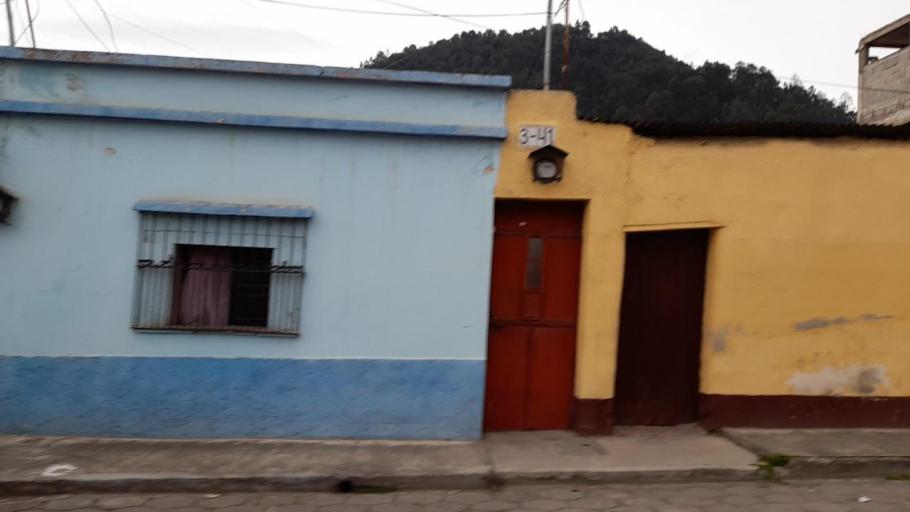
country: GT
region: Quetzaltenango
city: Quetzaltenango
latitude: 14.8327
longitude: -91.5100
